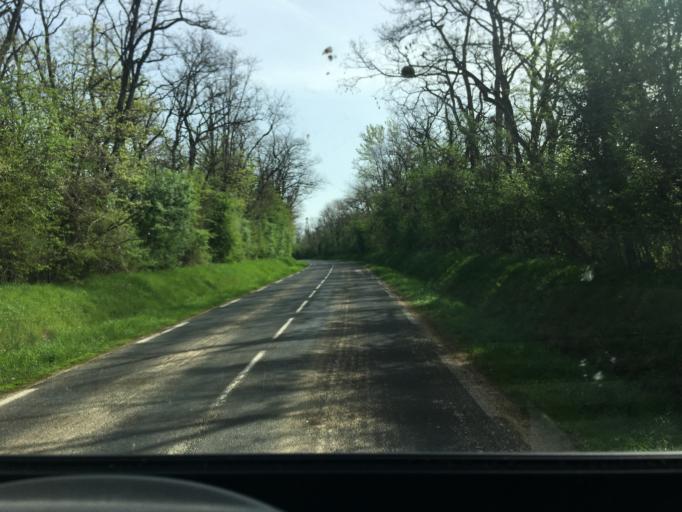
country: FR
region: Lorraine
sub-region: Departement de Meurthe-et-Moselle
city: Gondreville
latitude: 48.6614
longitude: 5.9874
